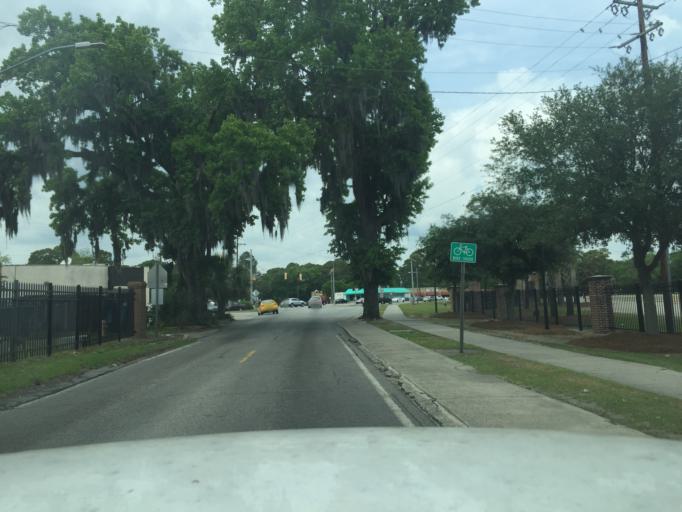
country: US
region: Georgia
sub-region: Chatham County
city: Thunderbolt
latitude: 32.0266
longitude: -81.0702
